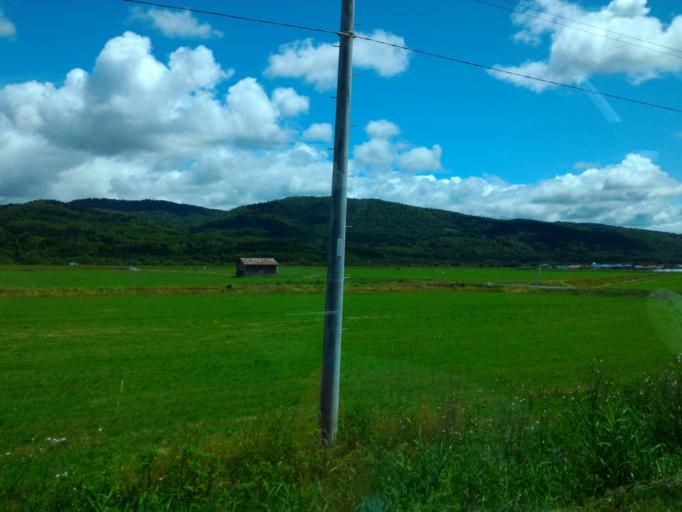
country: JP
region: Hokkaido
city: Nayoro
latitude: 44.5712
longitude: 142.3138
